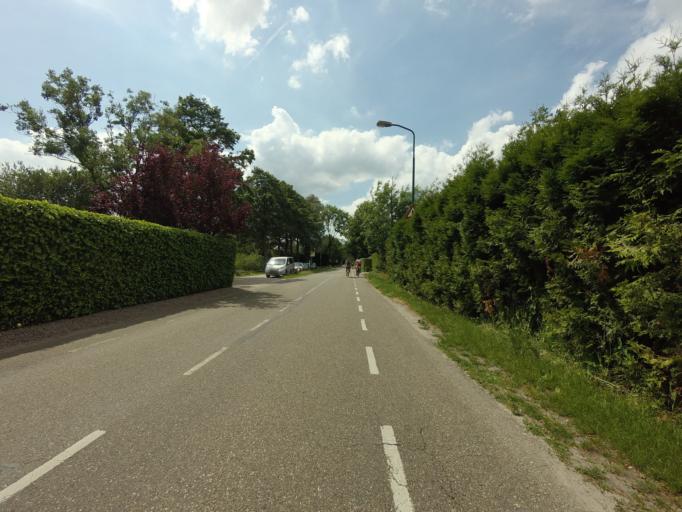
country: NL
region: North Holland
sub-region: Gemeente Wijdemeren
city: Oud-Loosdrecht
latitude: 52.1866
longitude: 5.0731
